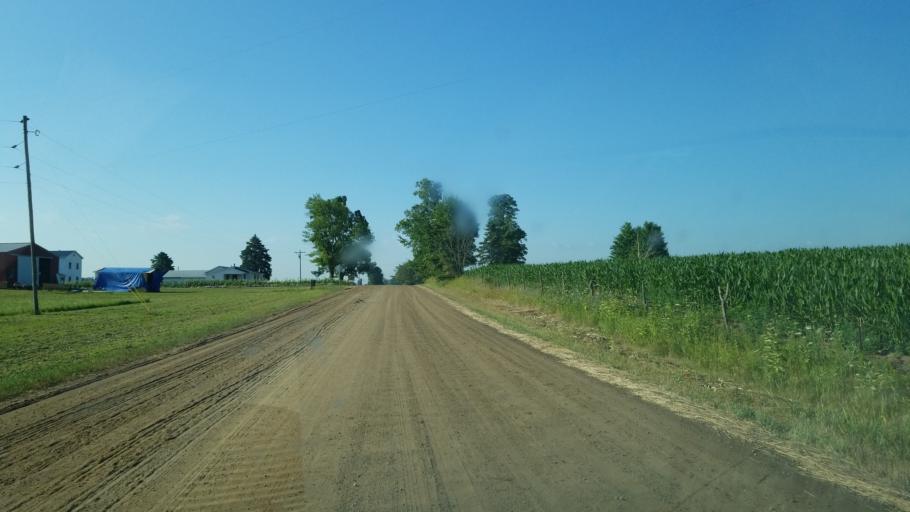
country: US
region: Michigan
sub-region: Mecosta County
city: Canadian Lakes
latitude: 43.5536
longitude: -85.3930
